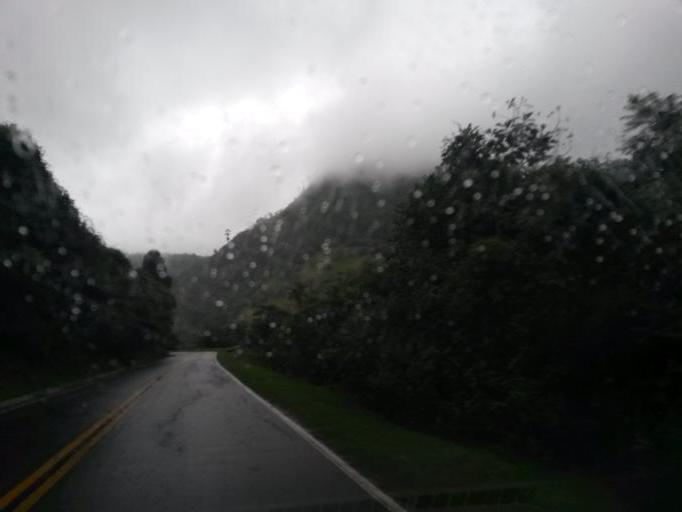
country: CO
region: Cauca
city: Popayan
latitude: 2.3699
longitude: -76.4928
